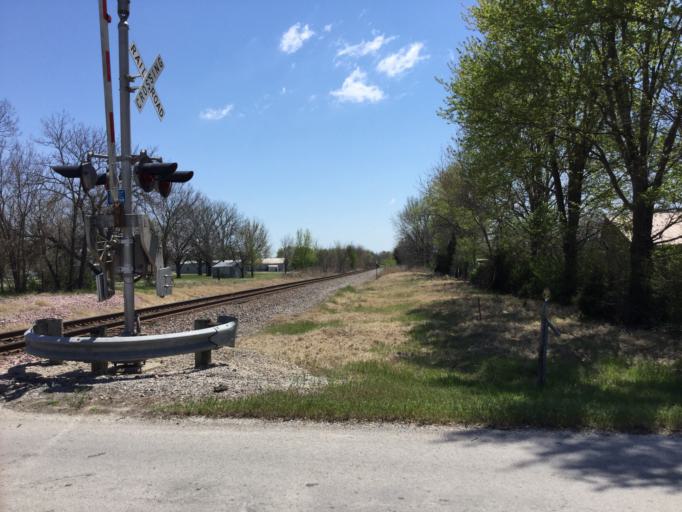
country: US
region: Kansas
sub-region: Montgomery County
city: Independence
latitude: 37.2364
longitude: -95.7255
